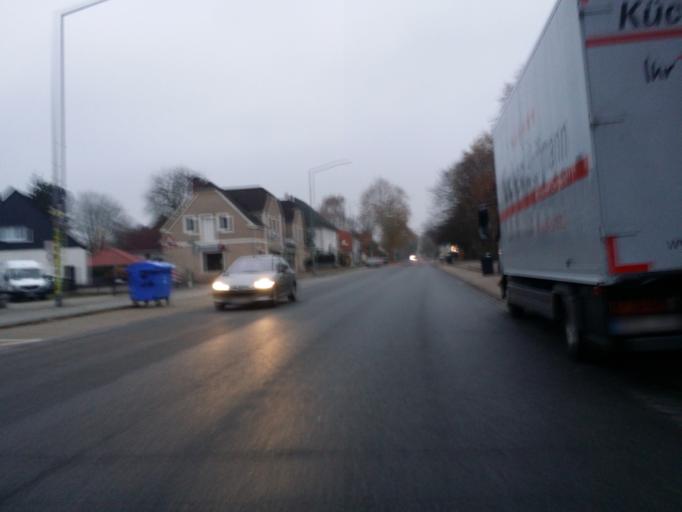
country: DE
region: Lower Saxony
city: Stuhr
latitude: 53.0104
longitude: 8.7877
